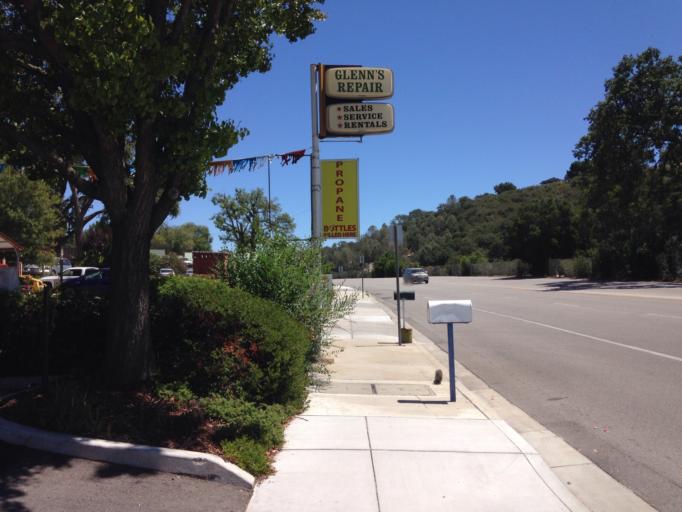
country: US
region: California
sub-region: San Luis Obispo County
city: Atascadero
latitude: 35.4952
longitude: -120.6793
